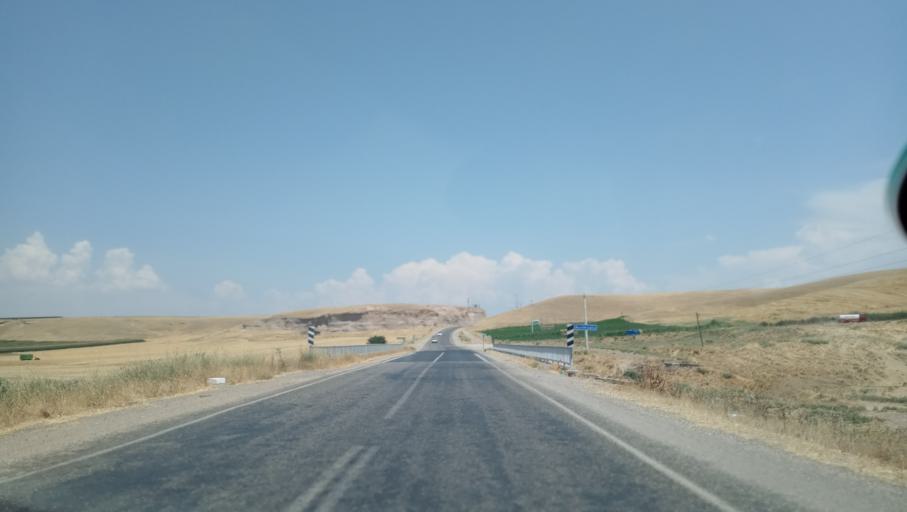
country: TR
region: Diyarbakir
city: Aralik
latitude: 37.8083
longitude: 40.7160
